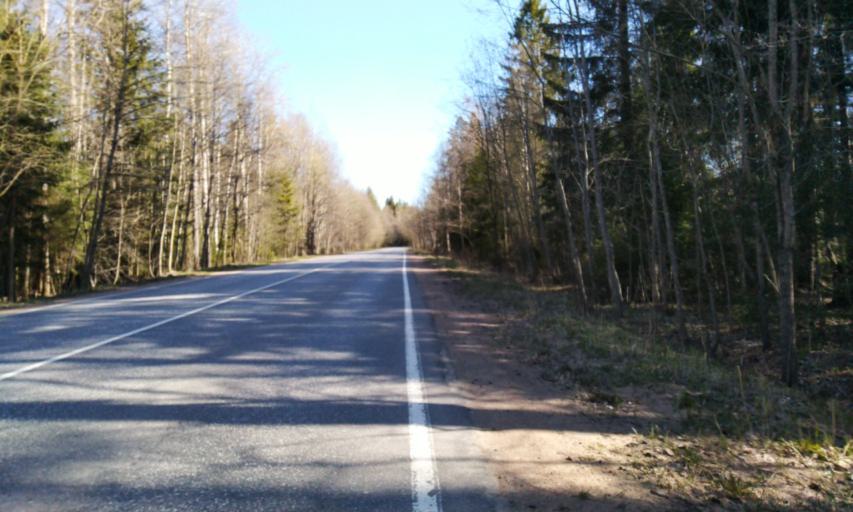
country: RU
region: Leningrad
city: Garbolovo
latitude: 60.3428
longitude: 30.4371
